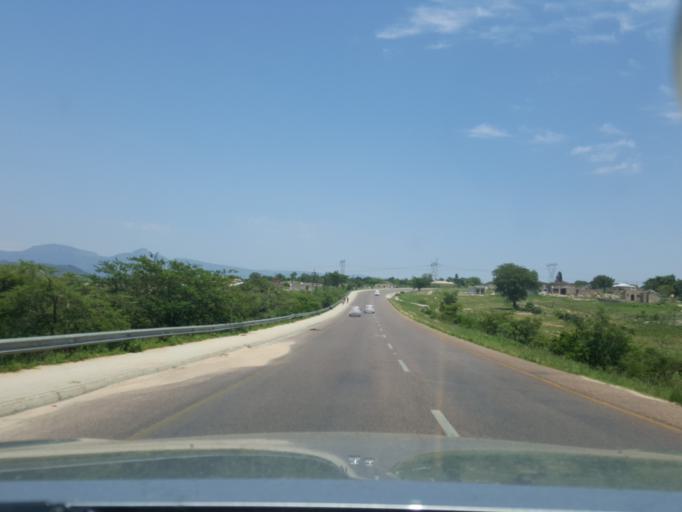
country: ZA
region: Limpopo
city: Thulamahashi
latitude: -24.7810
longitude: 31.0581
